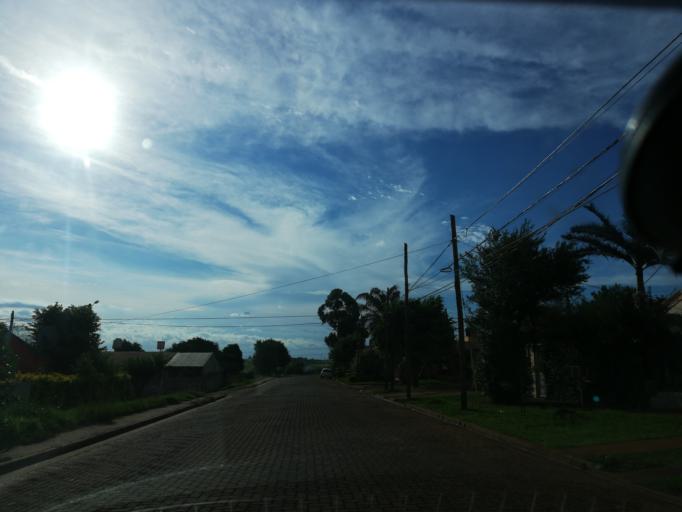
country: AR
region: Misiones
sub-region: Departamento de Capital
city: Posadas
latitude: -27.4203
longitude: -55.9522
